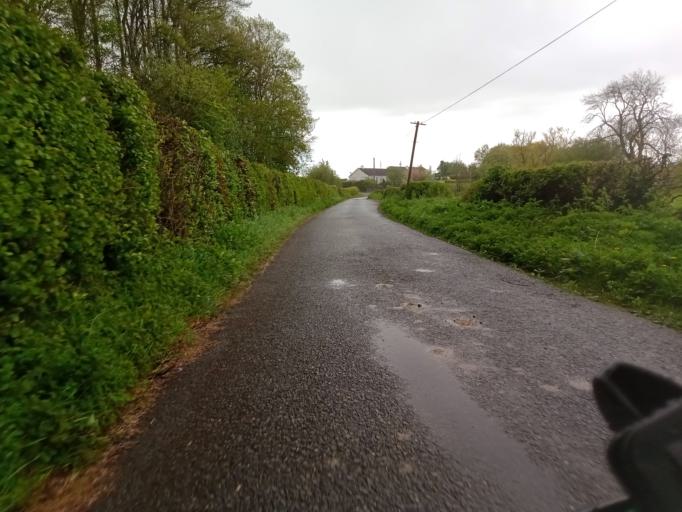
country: IE
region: Leinster
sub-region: Kilkenny
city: Kilkenny
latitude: 52.6851
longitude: -7.2683
